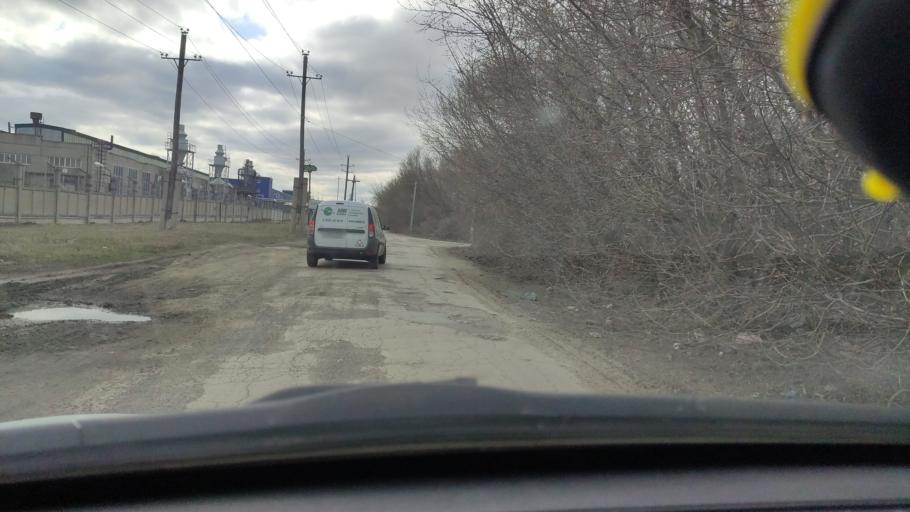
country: RU
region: Samara
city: Tol'yatti
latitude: 53.5255
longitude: 49.4569
